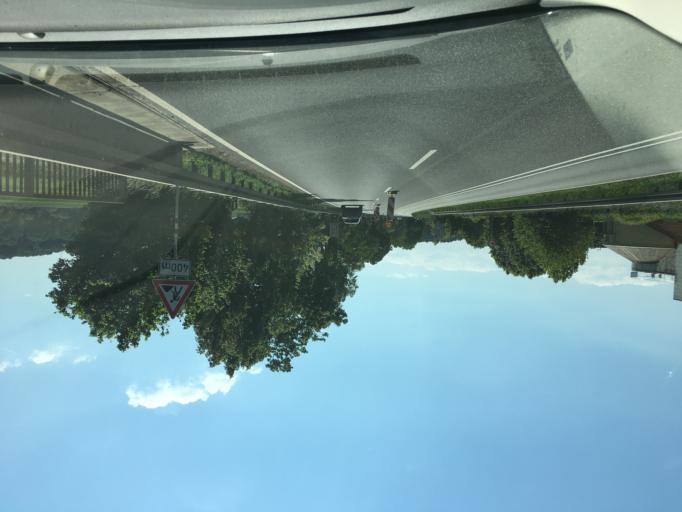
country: DE
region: Hesse
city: Bebra
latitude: 50.9740
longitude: 9.7811
